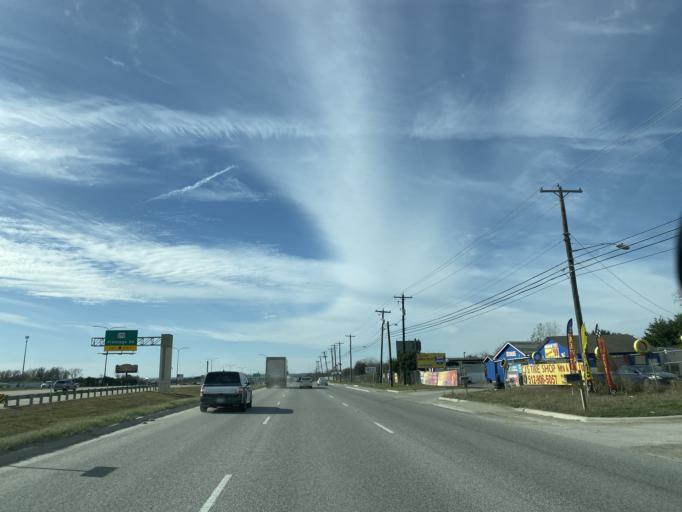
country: US
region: Texas
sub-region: Travis County
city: Manor
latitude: 30.3310
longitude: -97.6273
